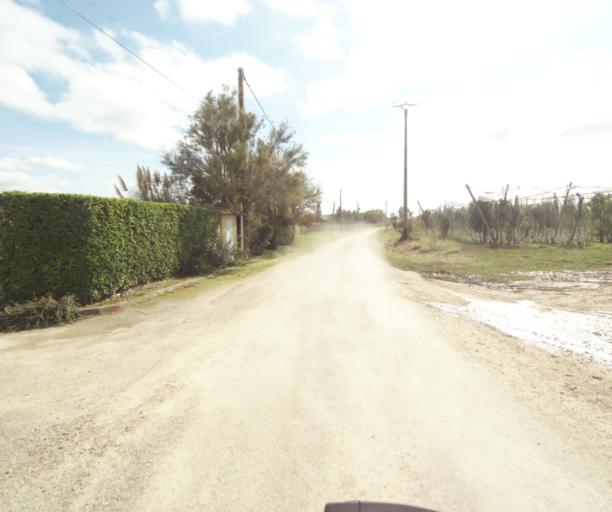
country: FR
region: Midi-Pyrenees
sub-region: Departement du Tarn-et-Garonne
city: Montech
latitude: 43.9422
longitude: 1.2064
